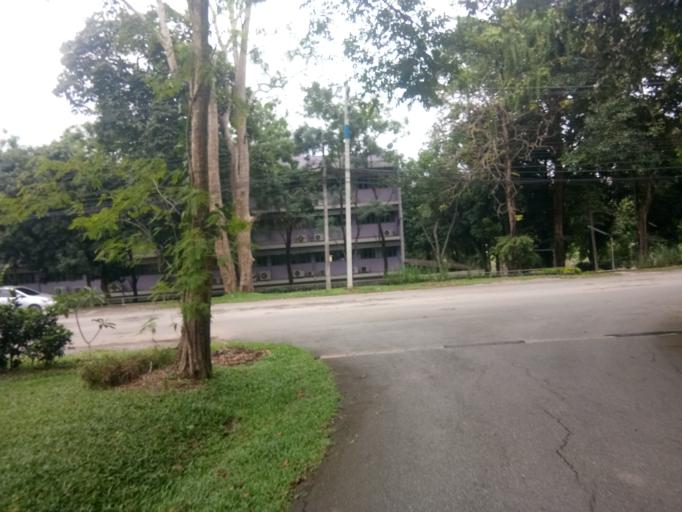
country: TH
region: Chiang Rai
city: Chiang Rai
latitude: 19.9810
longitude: 99.8493
